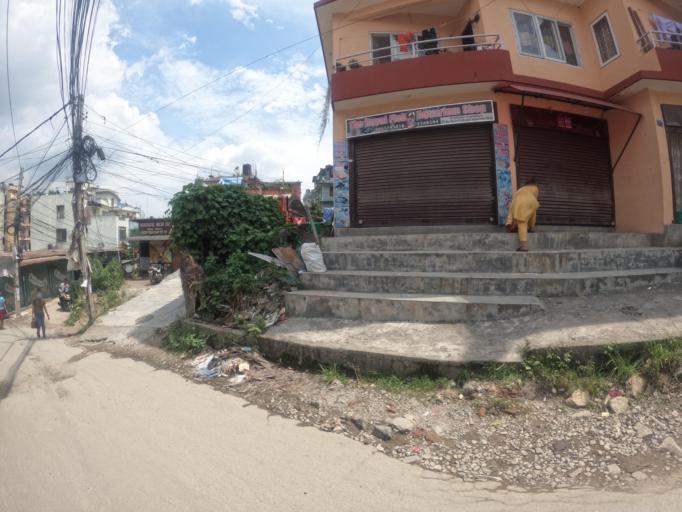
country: NP
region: Central Region
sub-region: Bagmati Zone
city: Patan
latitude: 27.6762
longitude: 85.3659
